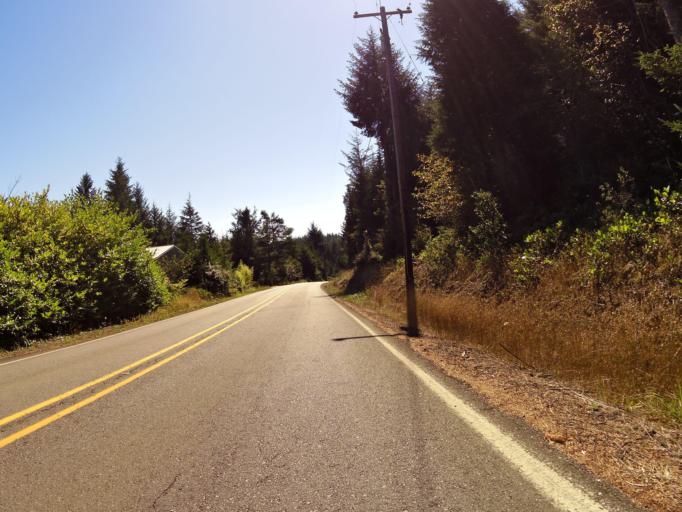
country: US
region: Oregon
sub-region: Coos County
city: Barview
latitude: 43.3267
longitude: -124.3415
